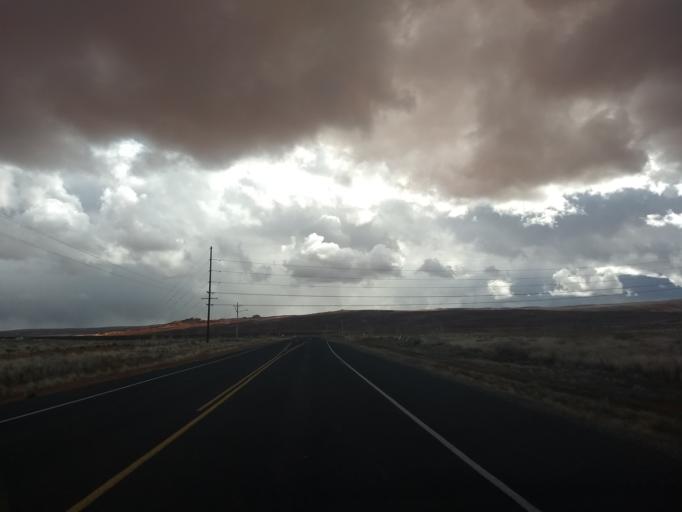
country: US
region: Utah
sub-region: Washington County
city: Hurricane
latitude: 37.1243
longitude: -113.3927
